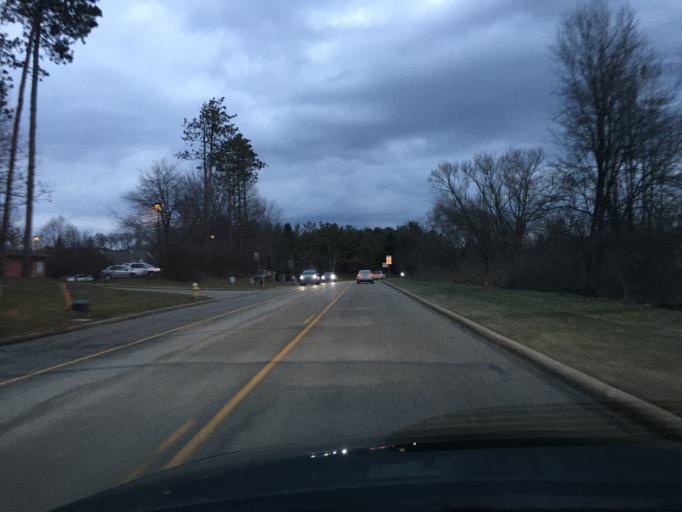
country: US
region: Ohio
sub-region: Summit County
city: Montrose-Ghent
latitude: 41.1489
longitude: -81.6387
